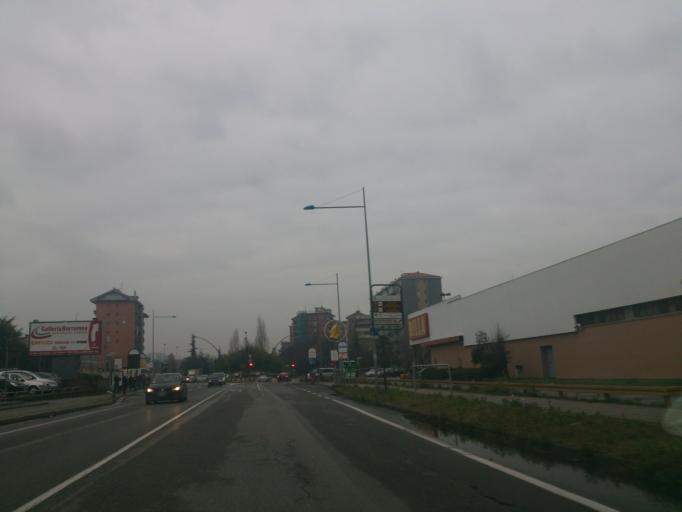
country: IT
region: Lombardy
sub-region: Citta metropolitana di Milano
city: San Donato Milanese
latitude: 45.4085
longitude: 9.2698
